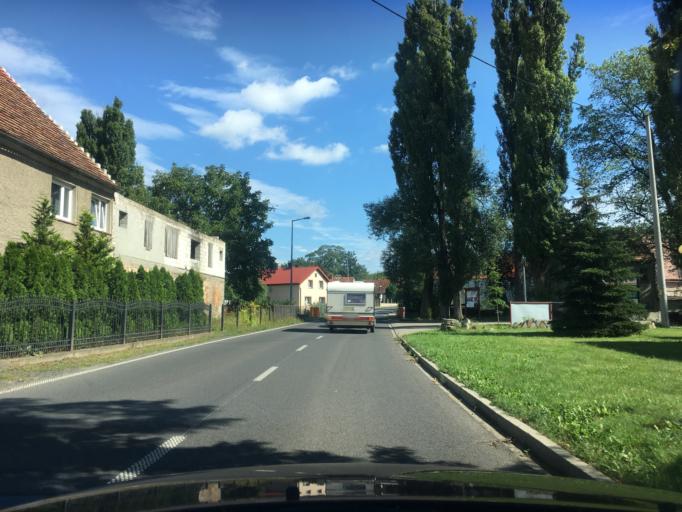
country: PL
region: Lower Silesian Voivodeship
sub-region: Powiat zgorzelecki
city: Piensk
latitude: 51.2272
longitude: 15.0282
